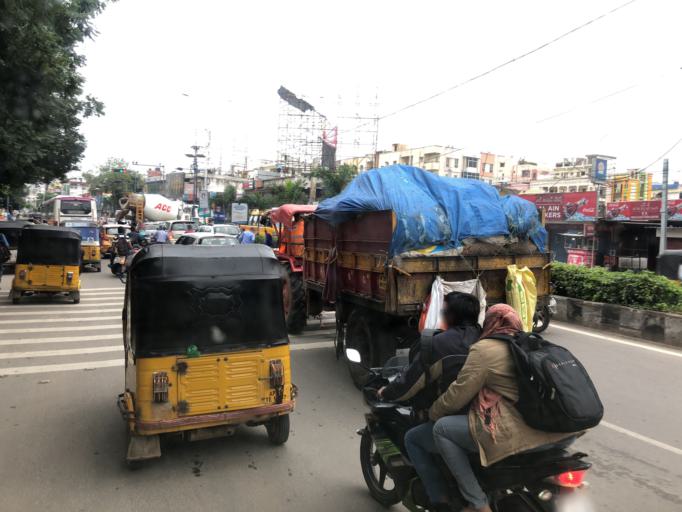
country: IN
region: Telangana
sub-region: Rangareddi
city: Kukatpalli
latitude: 17.4647
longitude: 78.3674
